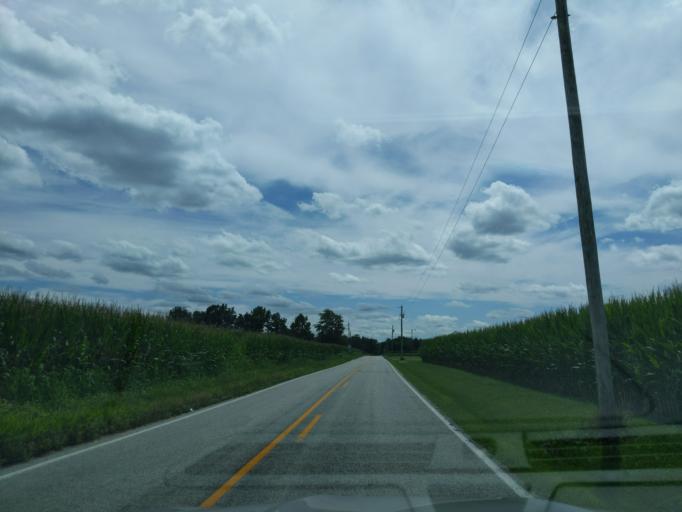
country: US
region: Indiana
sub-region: Ripley County
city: Osgood
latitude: 39.2053
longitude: -85.2776
